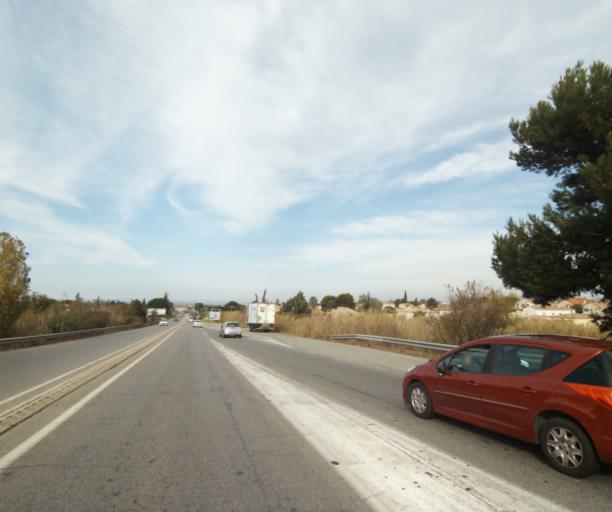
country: FR
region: Provence-Alpes-Cote d'Azur
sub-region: Departement des Bouches-du-Rhone
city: Gignac-la-Nerthe
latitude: 43.3826
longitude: 5.2209
